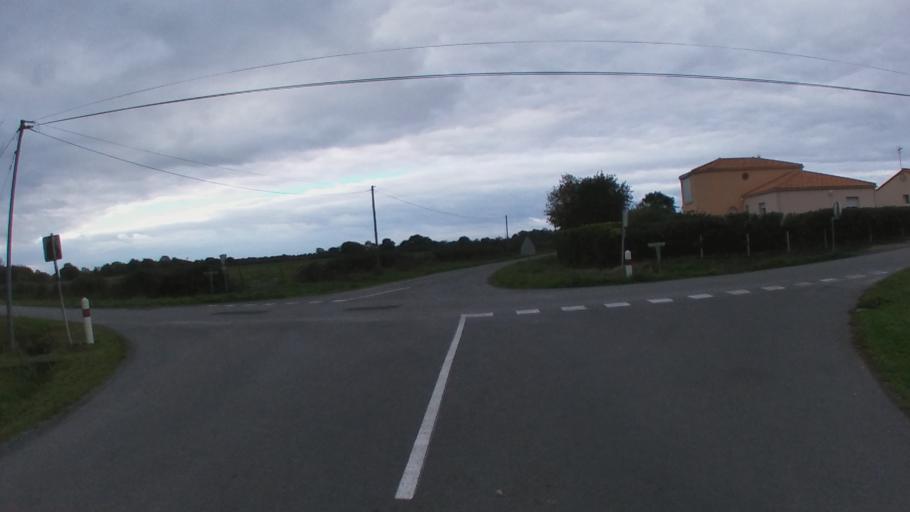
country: FR
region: Pays de la Loire
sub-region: Departement de la Loire-Atlantique
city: Corsept
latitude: 47.2716
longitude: -2.0760
